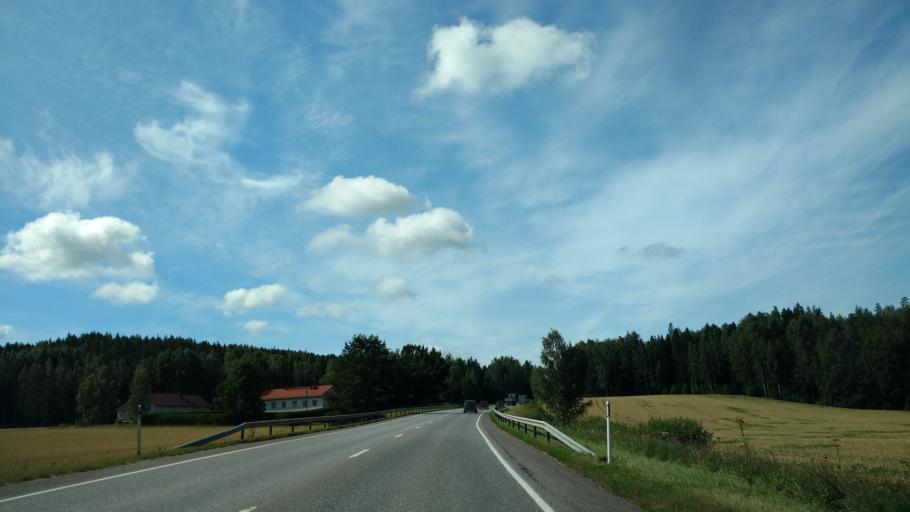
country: FI
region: Varsinais-Suomi
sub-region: Salo
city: Salo
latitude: 60.3480
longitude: 23.1398
